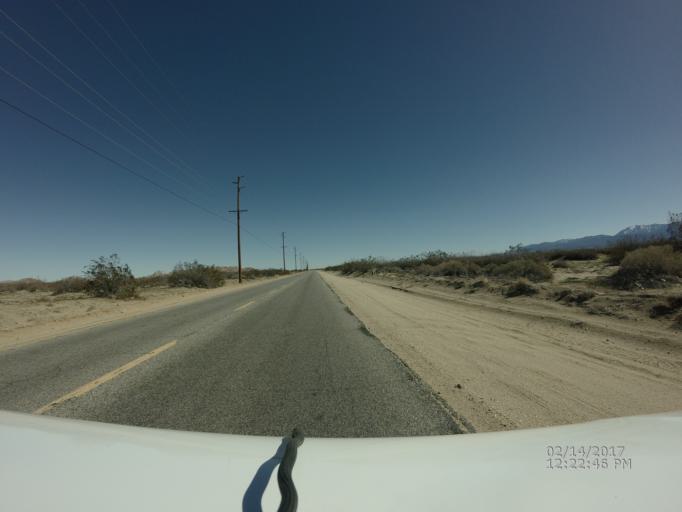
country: US
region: California
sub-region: Los Angeles County
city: Littlerock
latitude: 34.5799
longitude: -117.9225
